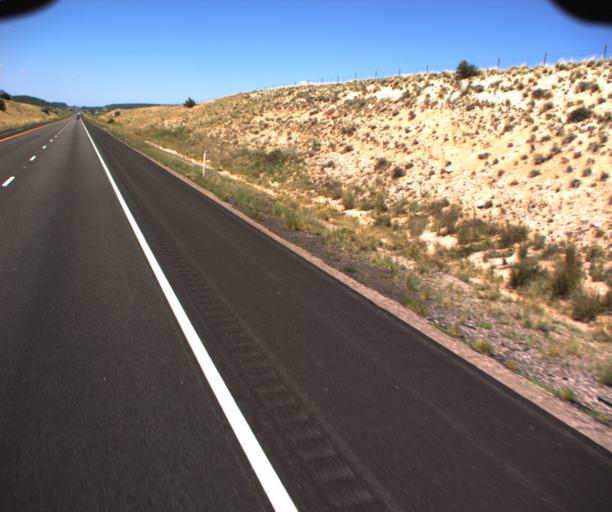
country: US
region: Arizona
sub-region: Mohave County
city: Peach Springs
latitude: 35.2659
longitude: -113.1539
